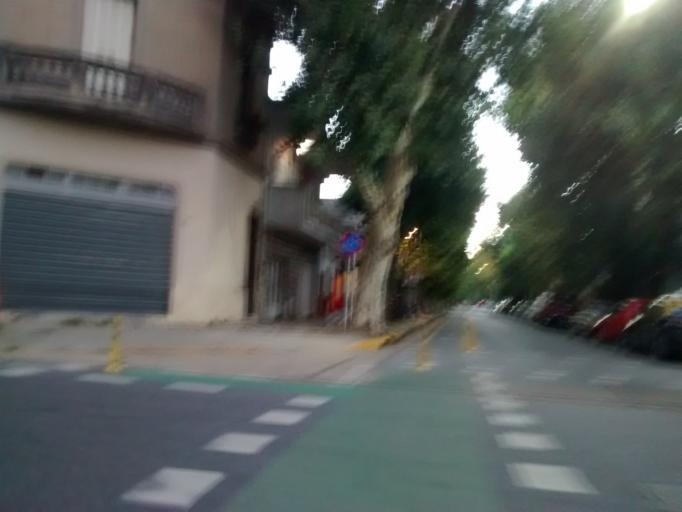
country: AR
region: Buenos Aires F.D.
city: Villa Santa Rita
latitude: -34.6076
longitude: -58.4578
